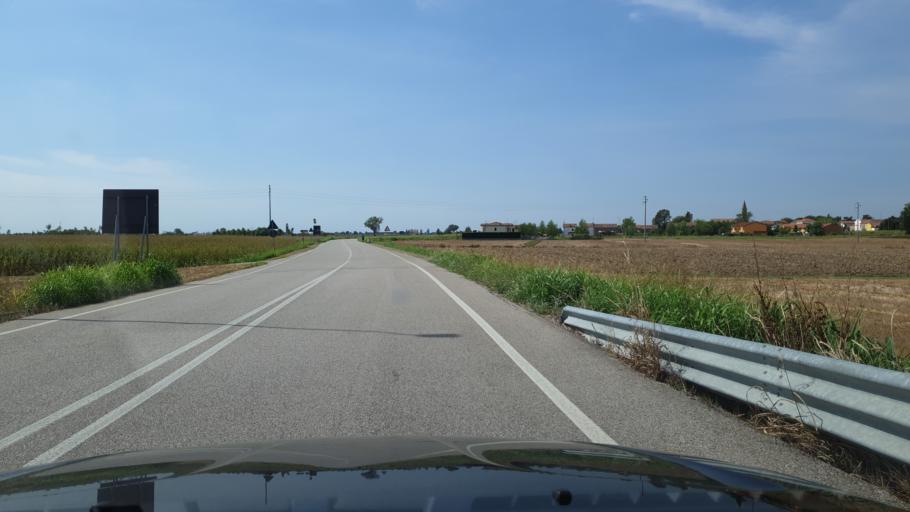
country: IT
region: Veneto
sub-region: Provincia di Rovigo
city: Pincara
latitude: 44.9982
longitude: 11.6159
